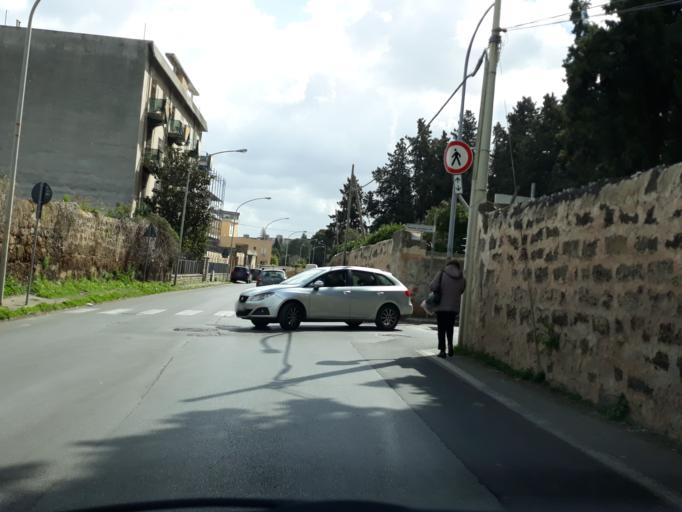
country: IT
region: Sicily
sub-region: Palermo
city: Palermo
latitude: 38.1250
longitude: 13.3158
